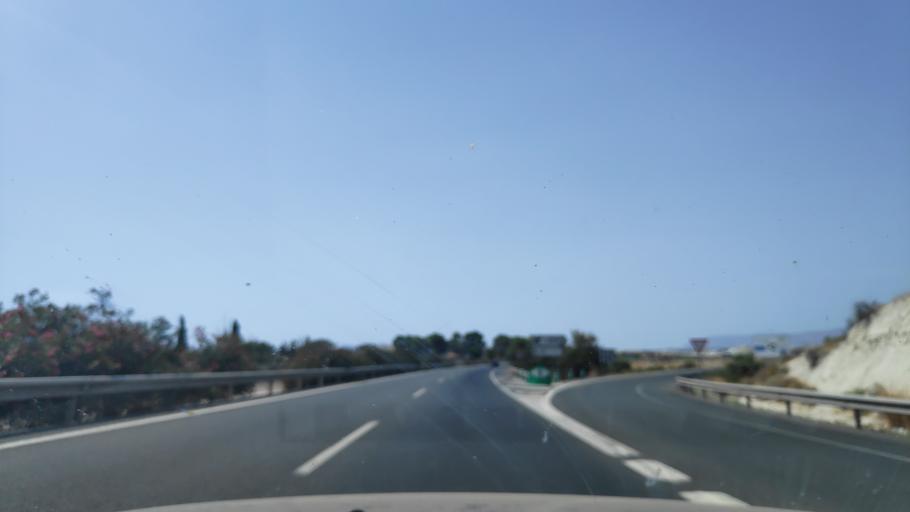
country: ES
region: Murcia
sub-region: Murcia
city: Molina de Segura
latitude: 38.0828
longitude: -1.2201
